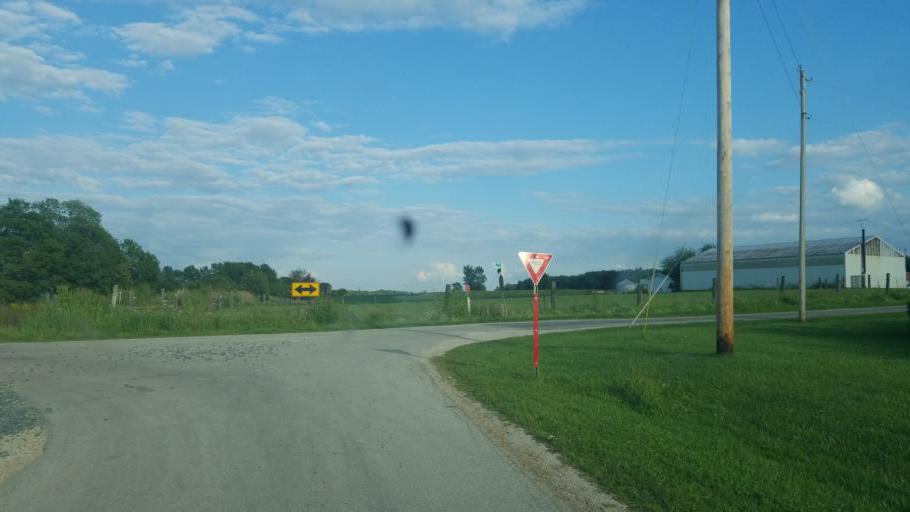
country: US
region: Ohio
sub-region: Sandusky County
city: Green Springs
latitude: 41.1098
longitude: -82.9963
